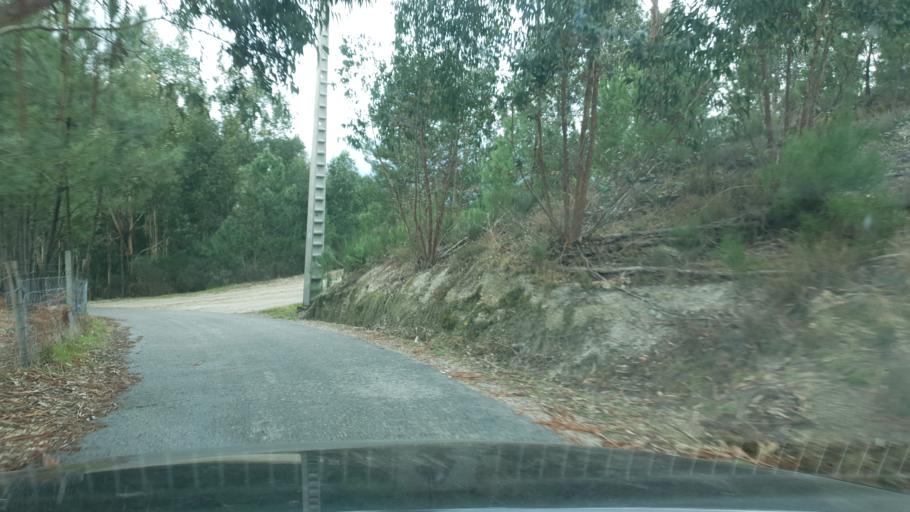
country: PT
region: Viseu
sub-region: Castro Daire
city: Castro Daire
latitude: 40.8794
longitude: -7.9940
